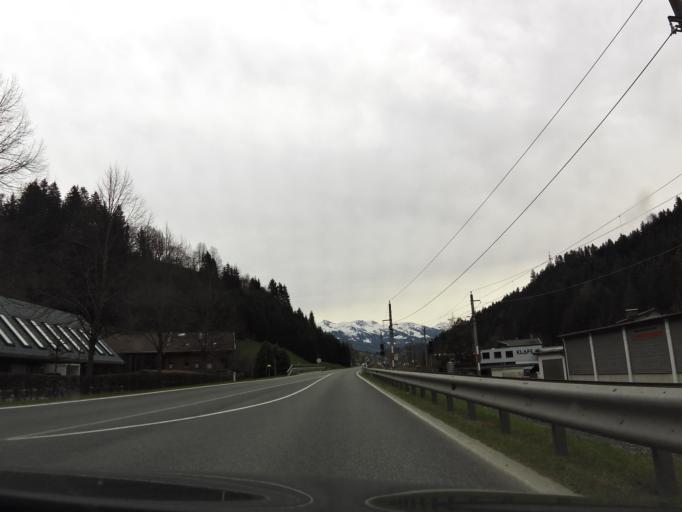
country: AT
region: Tyrol
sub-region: Politischer Bezirk Kitzbuhel
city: Itter
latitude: 47.4627
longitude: 12.1409
